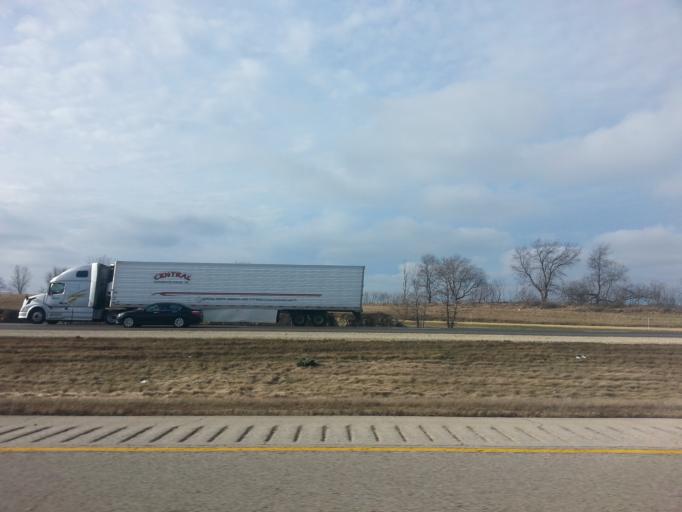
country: US
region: Illinois
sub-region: Ogle County
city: Davis Junction
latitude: 42.1683
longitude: -89.0234
